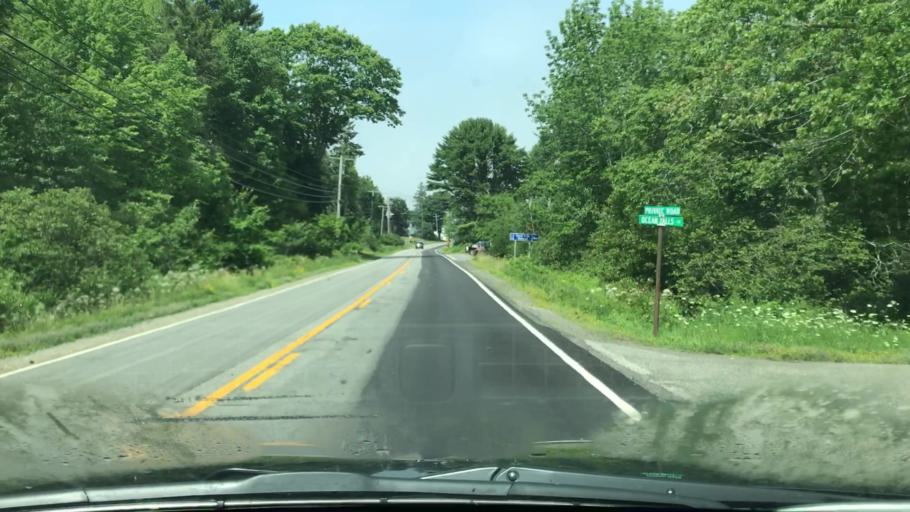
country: US
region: Maine
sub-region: Waldo County
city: Lincolnville
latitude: 44.2918
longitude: -69.0079
